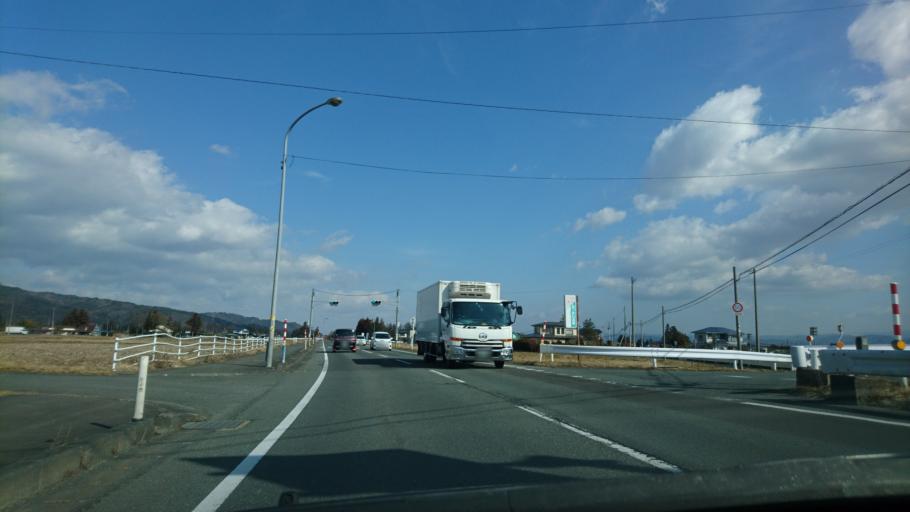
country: JP
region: Iwate
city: Morioka-shi
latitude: 39.5699
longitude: 141.1094
